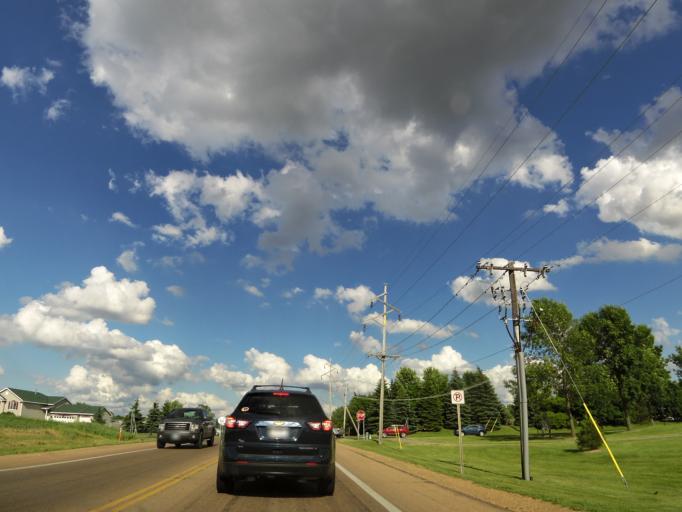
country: US
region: Minnesota
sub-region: Carver County
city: Waconia
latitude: 44.8406
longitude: -93.8093
